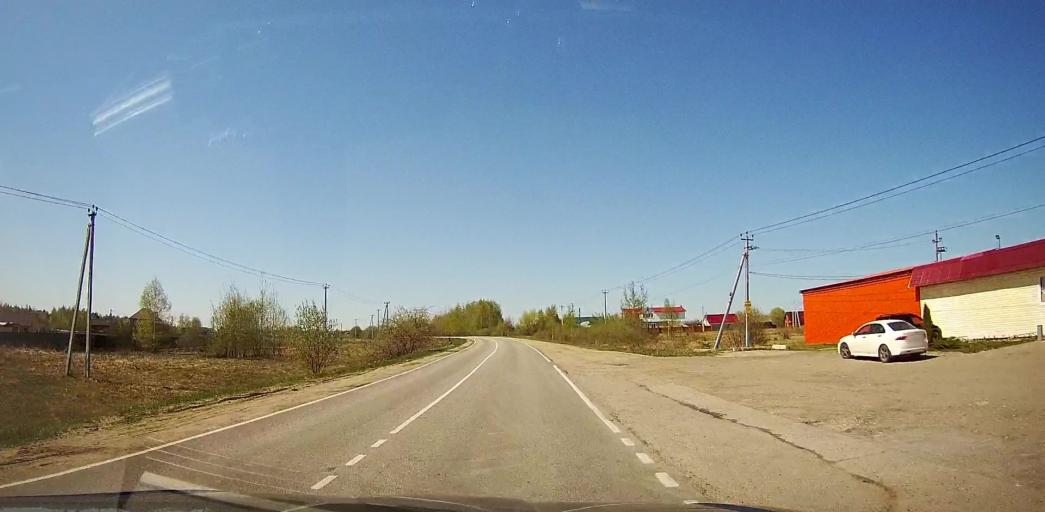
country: RU
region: Moskovskaya
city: Bronnitsy
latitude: 55.4554
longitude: 38.2945
